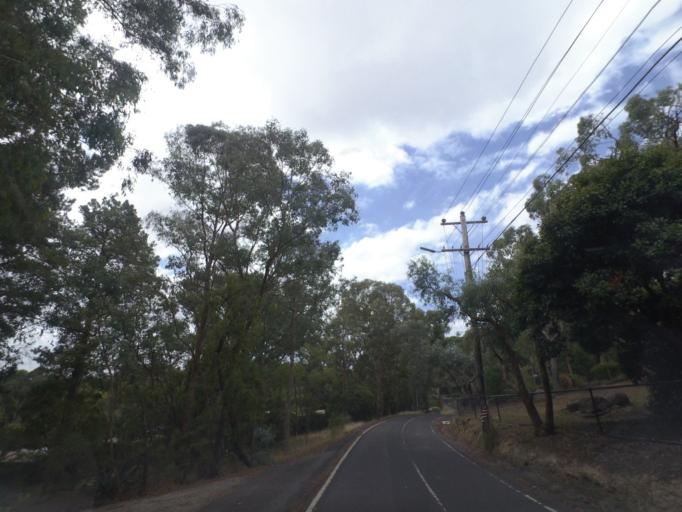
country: AU
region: Victoria
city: Mitcham
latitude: -37.7994
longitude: 145.2068
